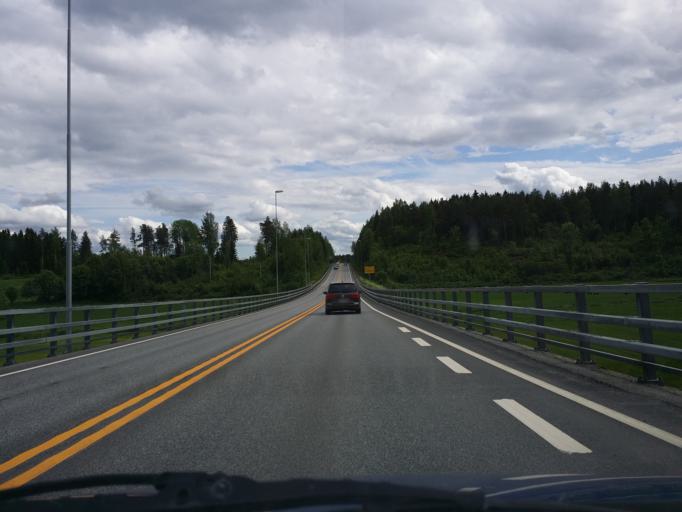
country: NO
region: Hedmark
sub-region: Stange
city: Stange
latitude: 60.7220
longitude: 11.2339
